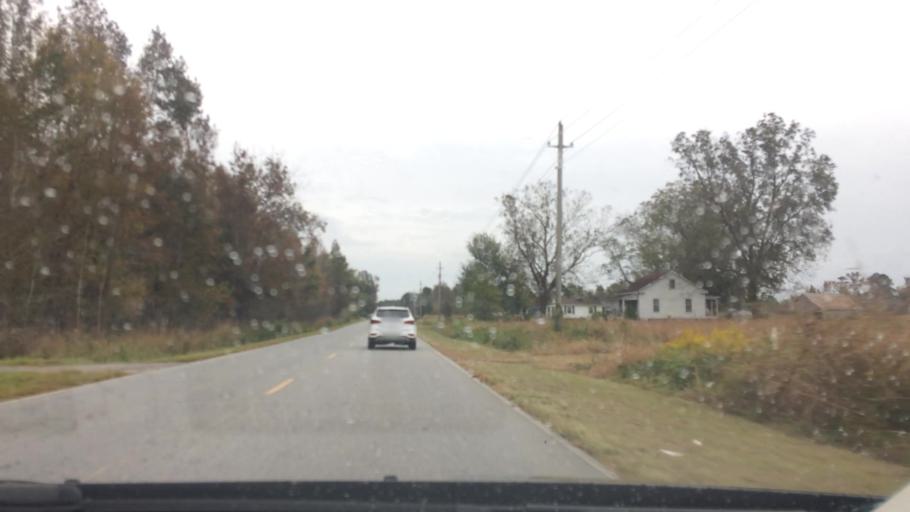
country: US
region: North Carolina
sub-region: Pitt County
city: Grifton
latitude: 35.4033
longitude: -77.4163
